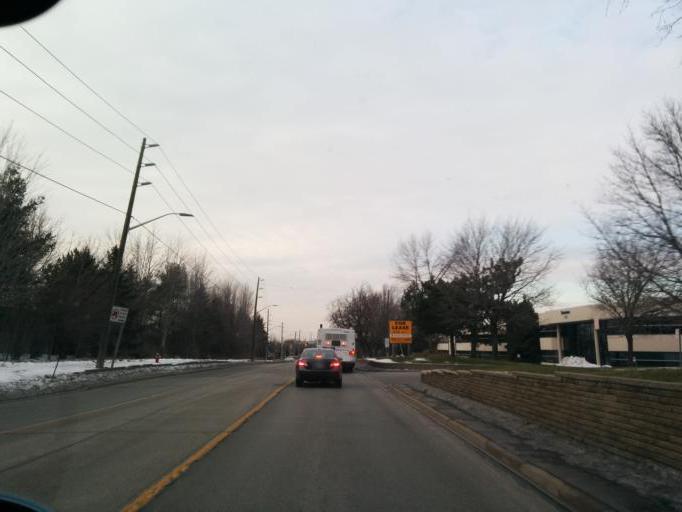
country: CA
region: Ontario
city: Mississauga
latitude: 43.6115
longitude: -79.6827
